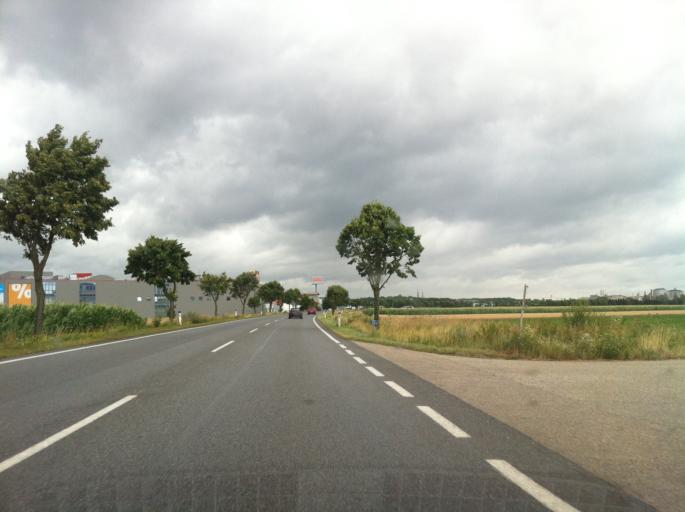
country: AT
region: Lower Austria
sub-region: Politischer Bezirk Tulln
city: Langenrohr
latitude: 48.3145
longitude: 16.0170
